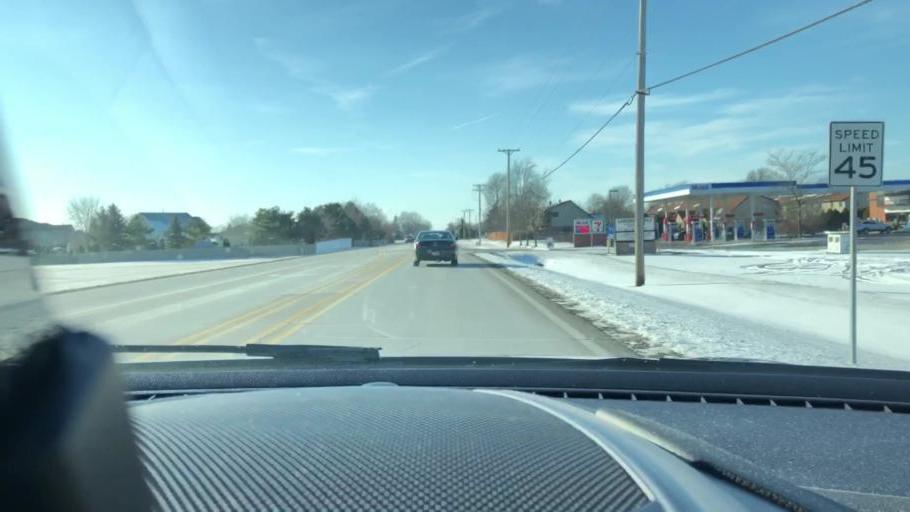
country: US
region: Illinois
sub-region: Will County
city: New Lenox
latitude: 41.4829
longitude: -87.9846
